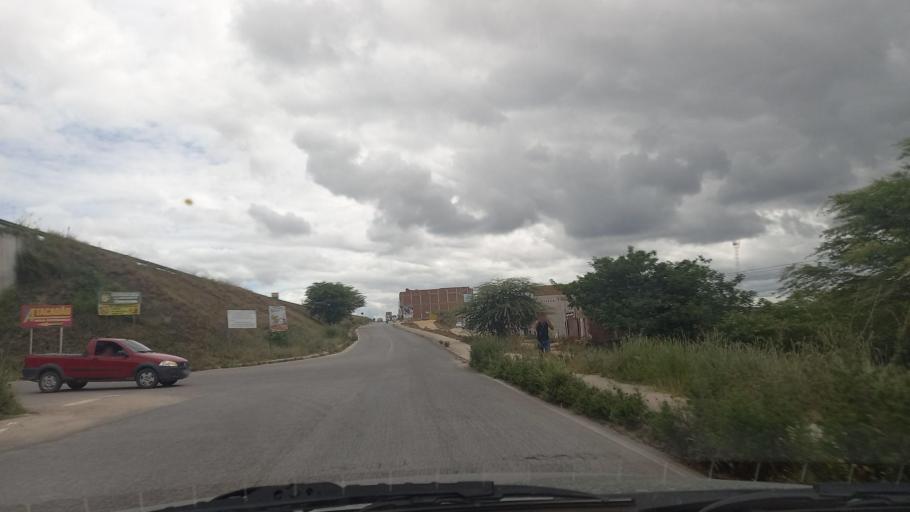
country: BR
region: Pernambuco
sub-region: Caruaru
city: Caruaru
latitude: -8.3313
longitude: -36.1270
